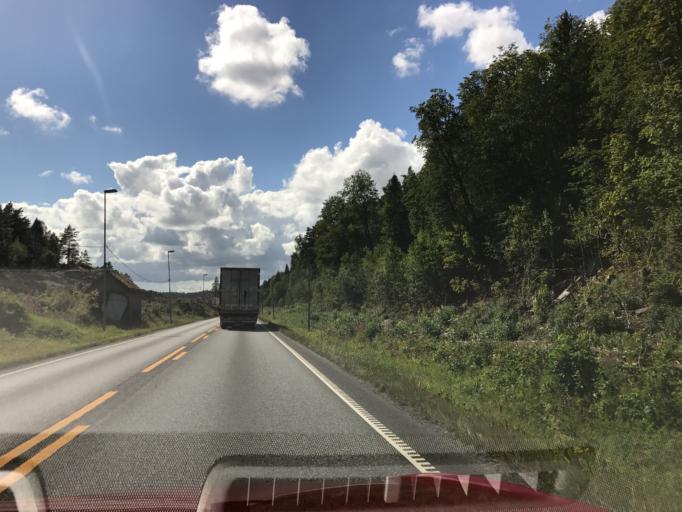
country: NO
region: Telemark
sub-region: Kragero
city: Kragero
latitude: 58.9717
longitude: 9.5074
